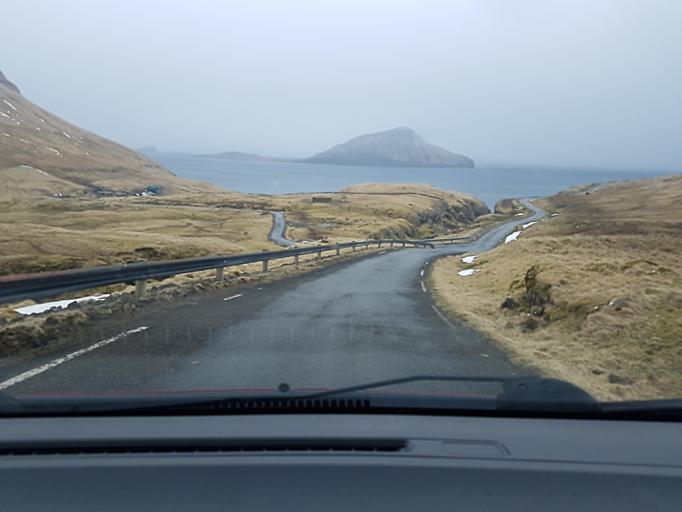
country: FO
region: Streymoy
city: Kollafjordhur
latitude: 62.0451
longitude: -6.9259
